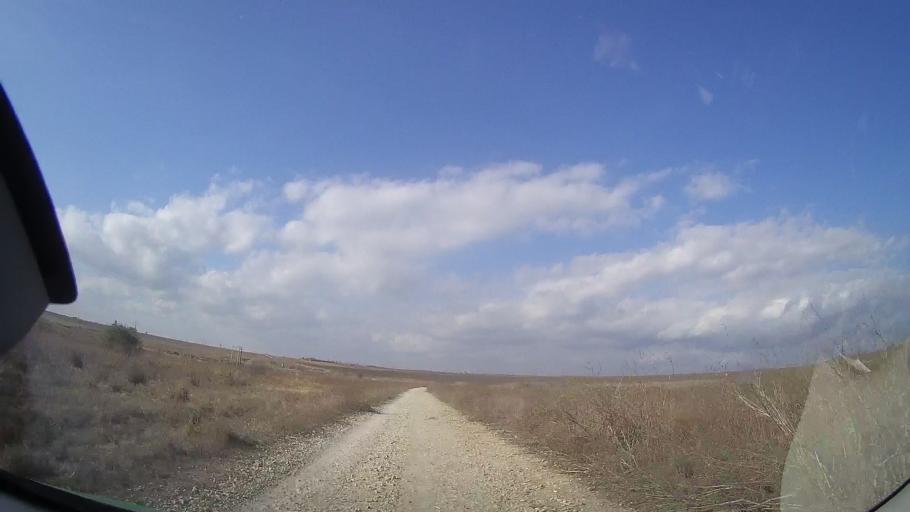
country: RO
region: Constanta
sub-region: Comuna Douazeci si Trei August
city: Douazeci si Trei August
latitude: 43.9080
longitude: 28.6101
